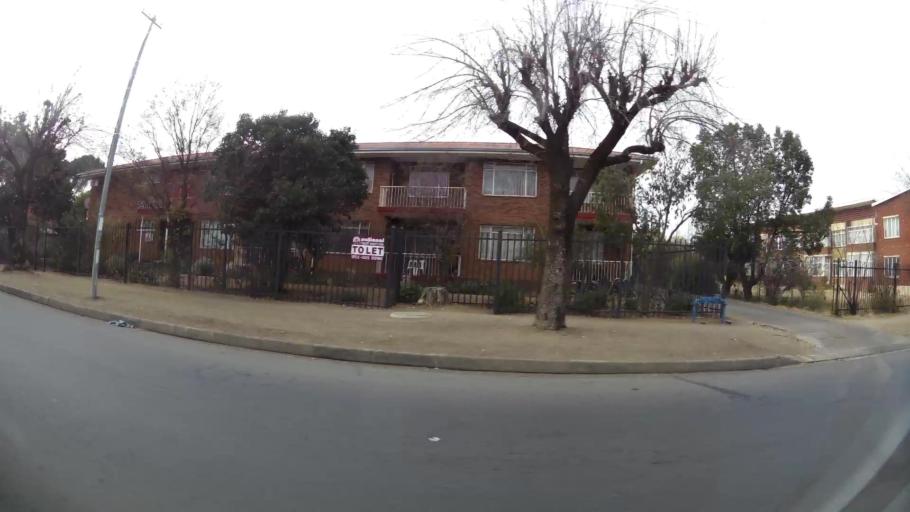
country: ZA
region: Orange Free State
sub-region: Mangaung Metropolitan Municipality
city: Bloemfontein
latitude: -29.1286
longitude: 26.2082
